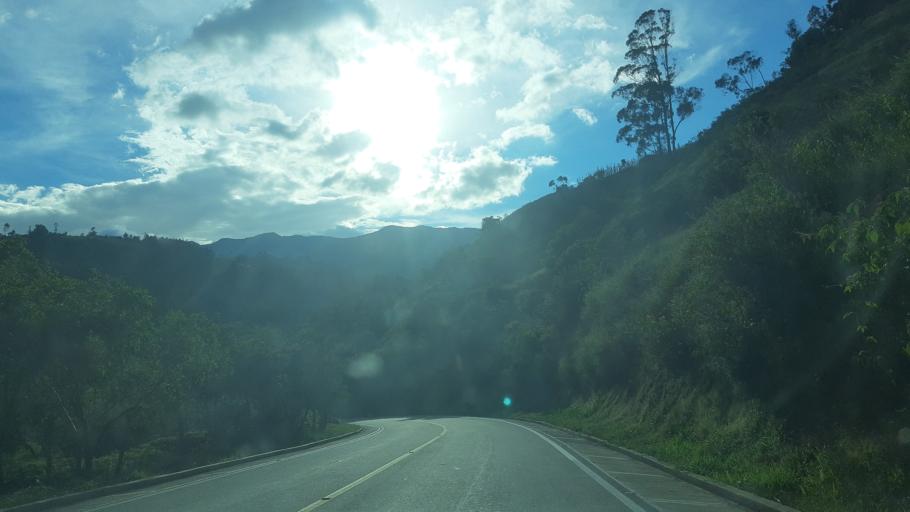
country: CO
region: Cundinamarca
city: Macheta
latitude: 5.0746
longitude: -73.5994
